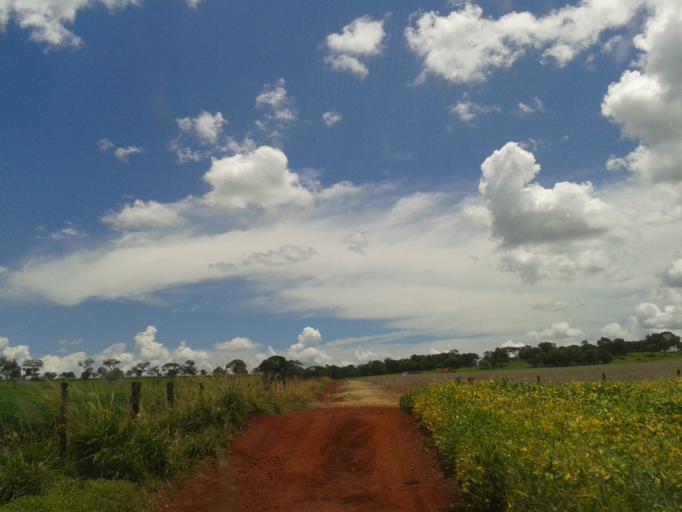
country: BR
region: Minas Gerais
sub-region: Capinopolis
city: Capinopolis
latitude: -18.7628
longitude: -49.7959
